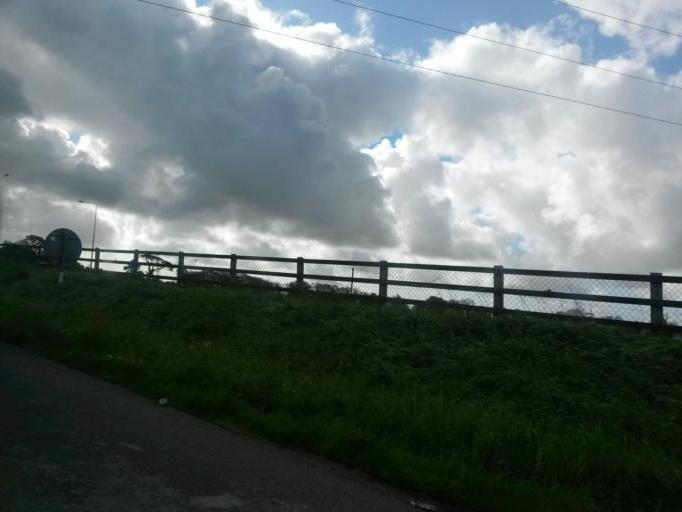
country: IE
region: Leinster
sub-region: Loch Garman
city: Gorey
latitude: 52.6329
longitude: -6.3746
